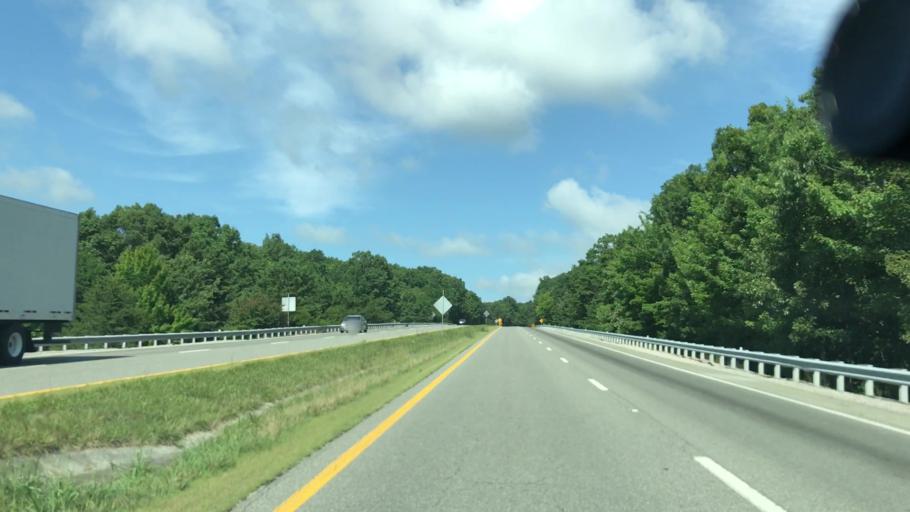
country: US
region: Virginia
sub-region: Montgomery County
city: Blacksburg
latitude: 37.2790
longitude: -80.4339
